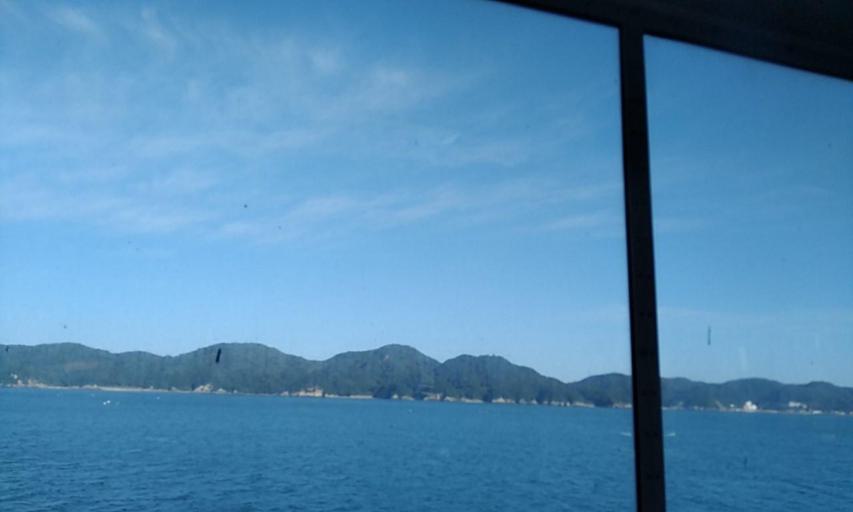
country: JP
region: Mie
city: Toba
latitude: 34.5041
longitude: 136.8848
